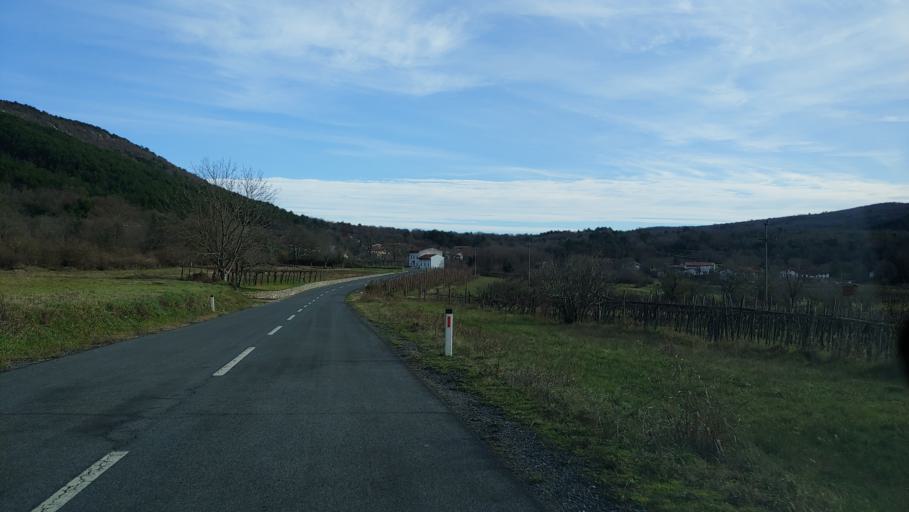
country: IT
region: Friuli Venezia Giulia
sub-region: Provincia di Trieste
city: Sistiana-Visogliano
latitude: 45.8127
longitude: 13.6364
